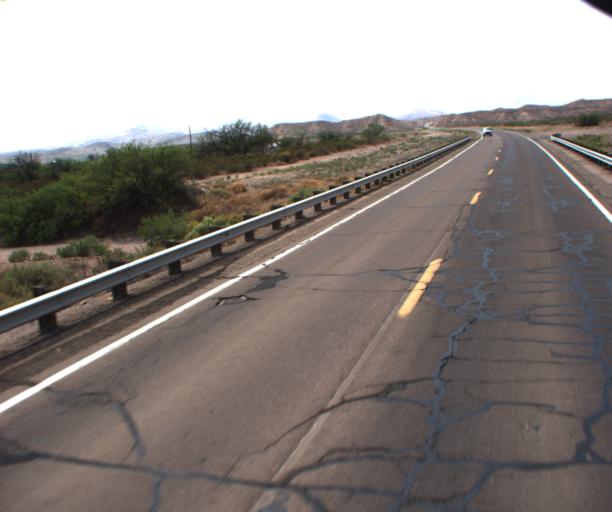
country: US
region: Arizona
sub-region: Greenlee County
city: Clifton
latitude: 32.7492
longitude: -109.1105
